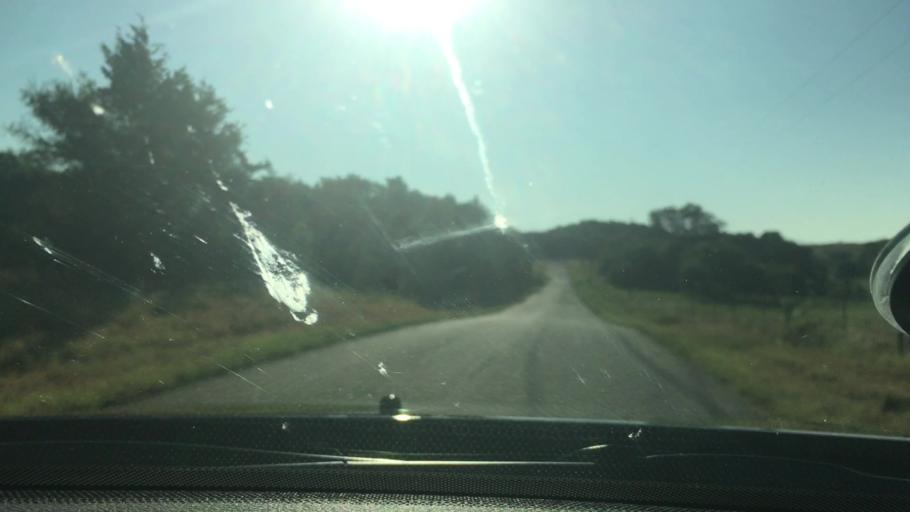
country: US
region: Oklahoma
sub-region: Murray County
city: Sulphur
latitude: 34.4049
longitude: -96.7969
